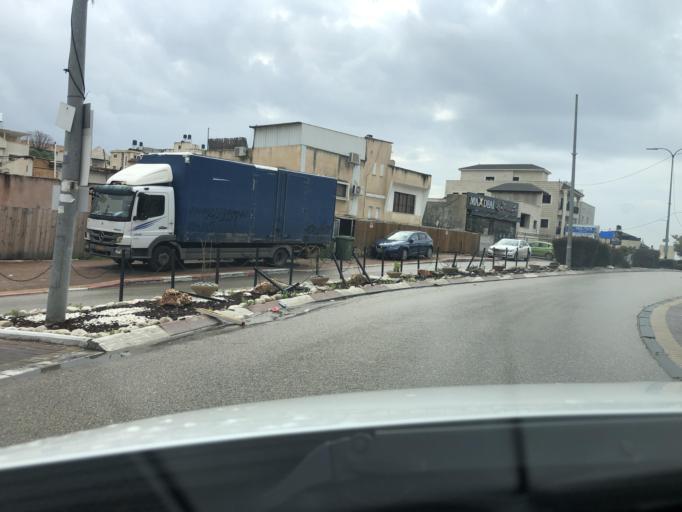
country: IL
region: Central District
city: Kafr Qasim
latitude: 32.1117
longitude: 34.9681
